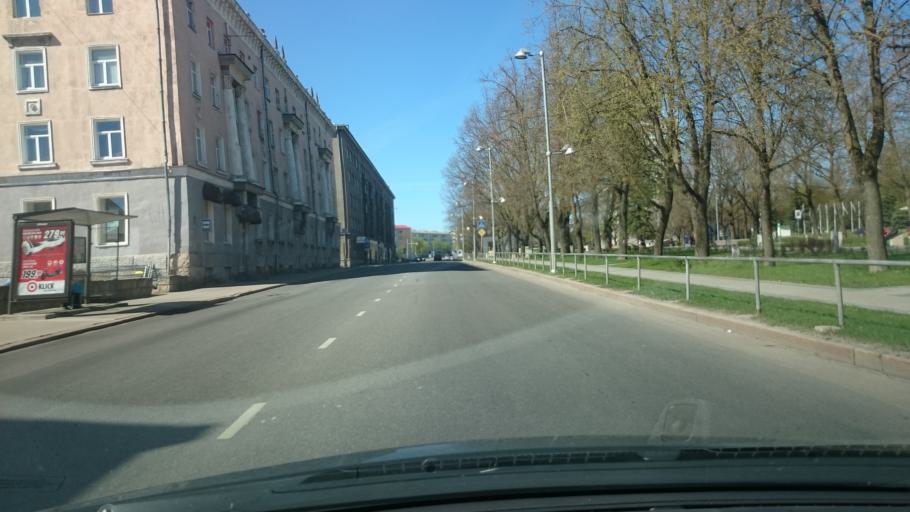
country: EE
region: Ida-Virumaa
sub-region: Narva linn
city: Narva
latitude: 59.3747
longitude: 28.1945
